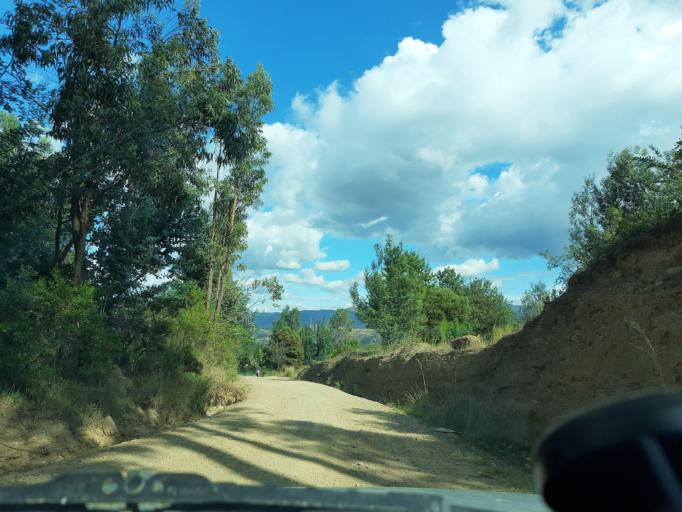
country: CO
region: Boyaca
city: Raquira
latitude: 5.5335
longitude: -73.6503
